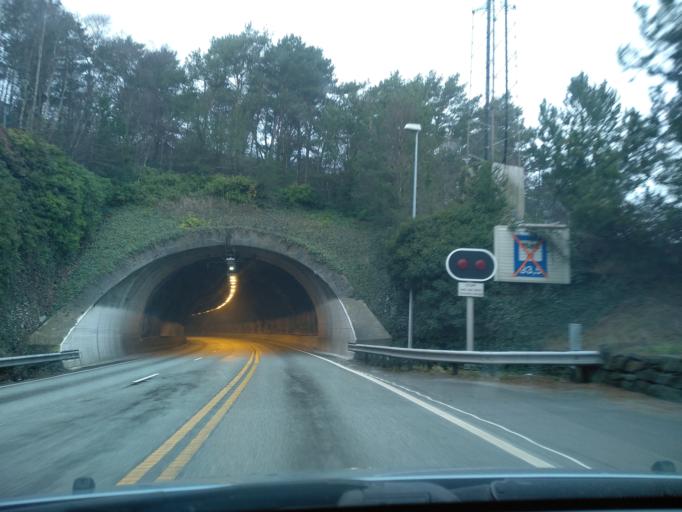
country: NO
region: Rogaland
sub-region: Randaberg
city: Randaberg
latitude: 59.0157
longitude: 5.6333
